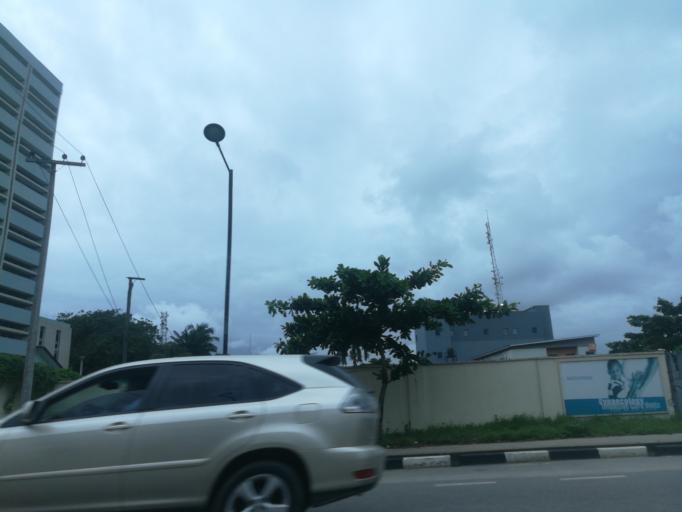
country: NG
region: Lagos
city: Lagos
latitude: 6.4440
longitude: 3.4088
